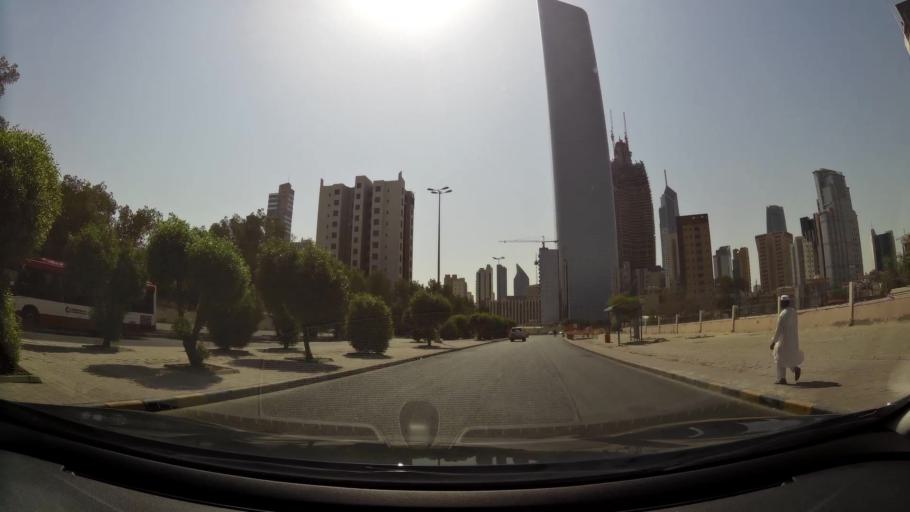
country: KW
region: Al Asimah
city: Ad Dasmah
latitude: 29.3832
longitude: 47.9943
